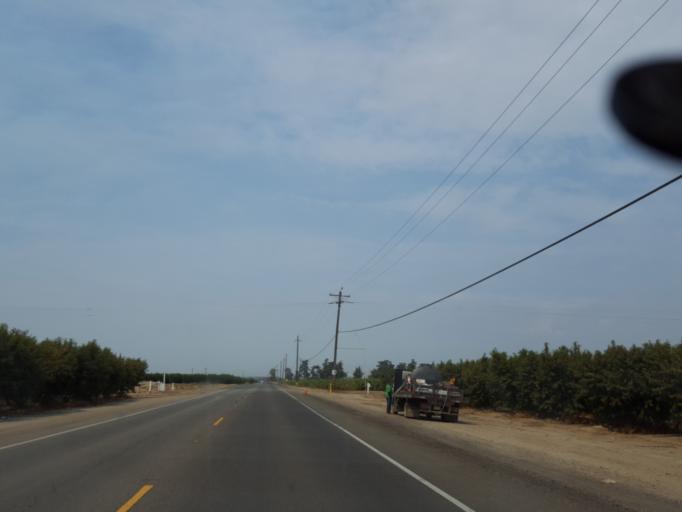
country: US
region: California
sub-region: Fresno County
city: Minkler
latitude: 36.6861
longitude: -119.4575
